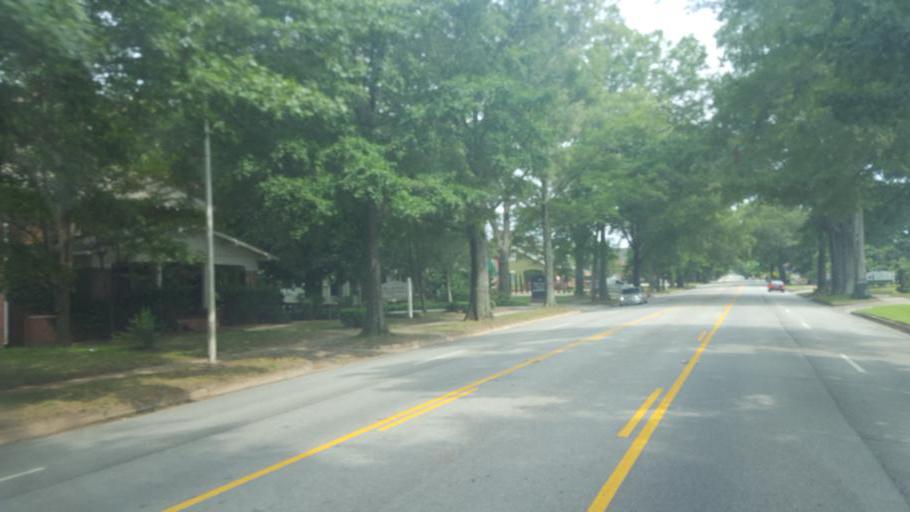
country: US
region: South Carolina
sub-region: York County
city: Rock Hill
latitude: 34.9334
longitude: -81.0259
